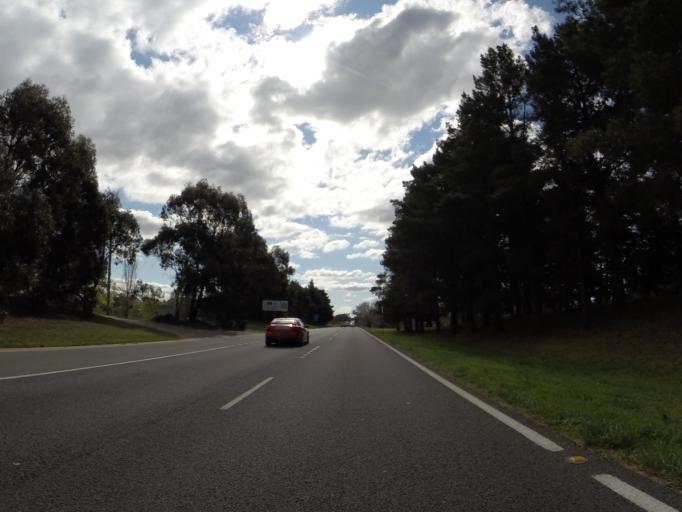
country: AU
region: Australian Capital Territory
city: Belconnen
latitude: -35.1971
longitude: 149.0892
